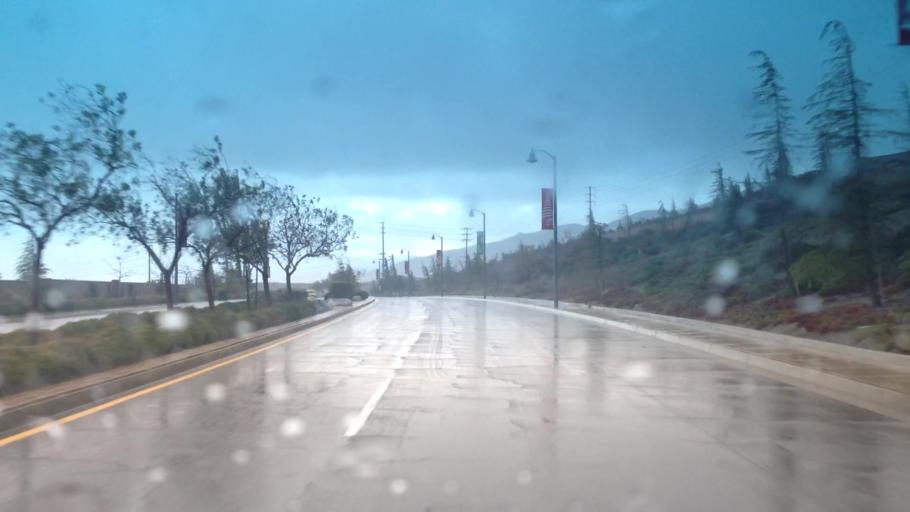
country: US
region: California
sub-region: Los Angeles County
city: Desert View Highlands
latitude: 34.5600
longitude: -118.1673
